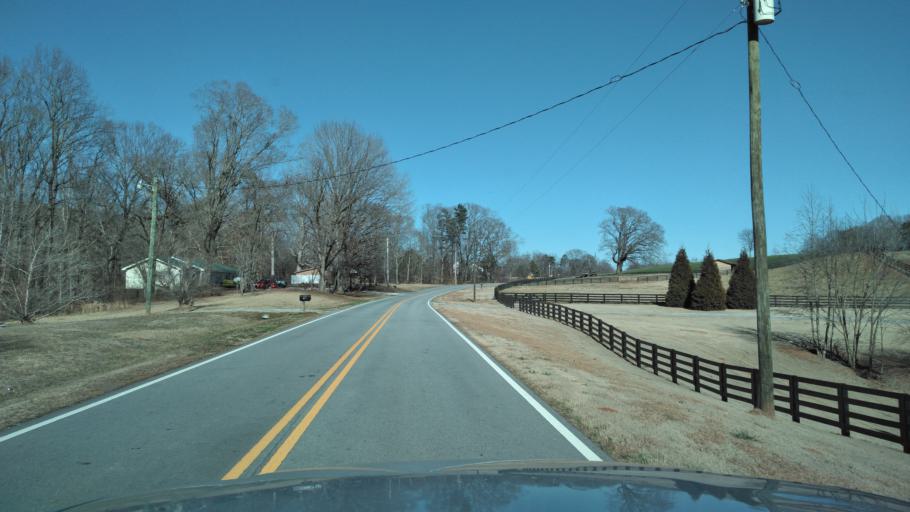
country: US
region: Georgia
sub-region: Hall County
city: Lula
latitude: 34.3143
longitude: -83.7182
